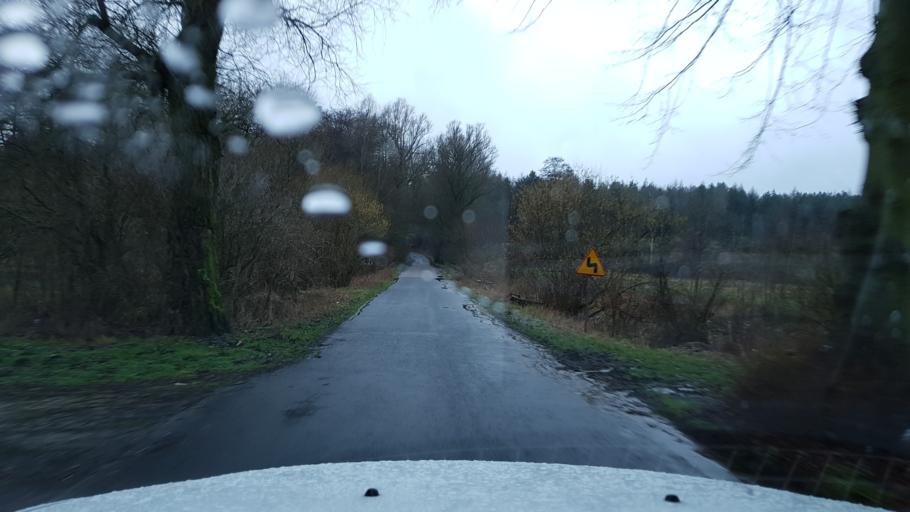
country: PL
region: West Pomeranian Voivodeship
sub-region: Powiat goleniowski
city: Osina
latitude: 53.5573
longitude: 15.0057
